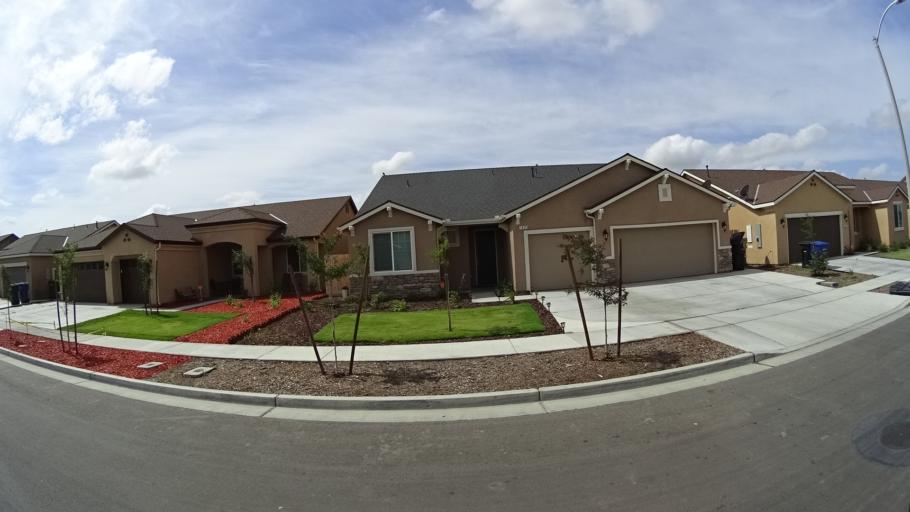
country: US
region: California
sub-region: Kings County
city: Hanford
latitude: 36.3077
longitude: -119.6711
